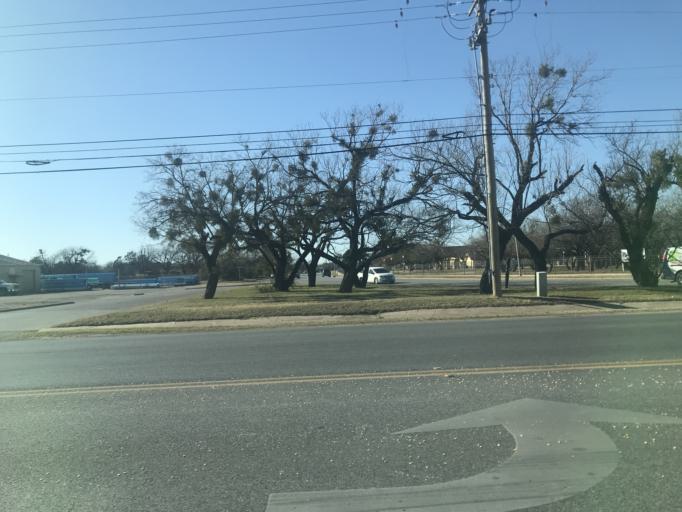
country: US
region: Texas
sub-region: Taylor County
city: Abilene
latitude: 32.4152
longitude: -99.7424
